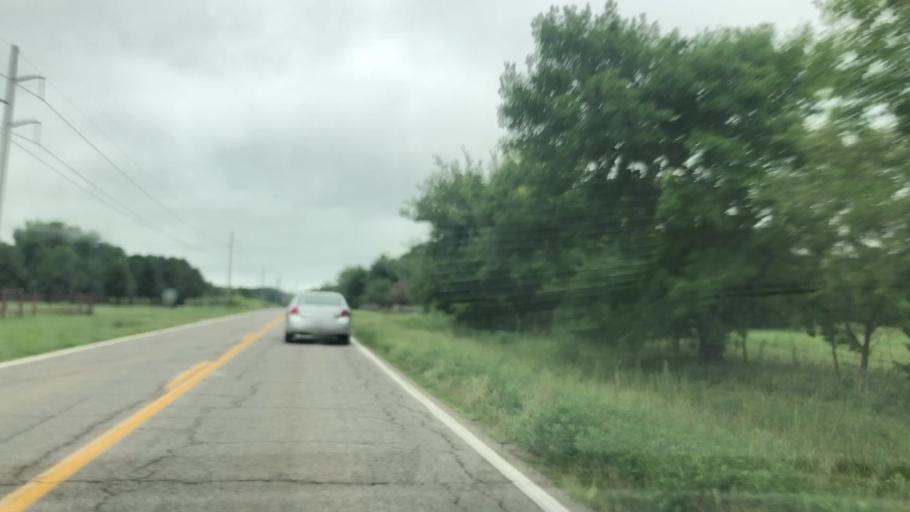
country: US
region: Oklahoma
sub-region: Washington County
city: Dewey
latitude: 36.7280
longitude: -95.8405
